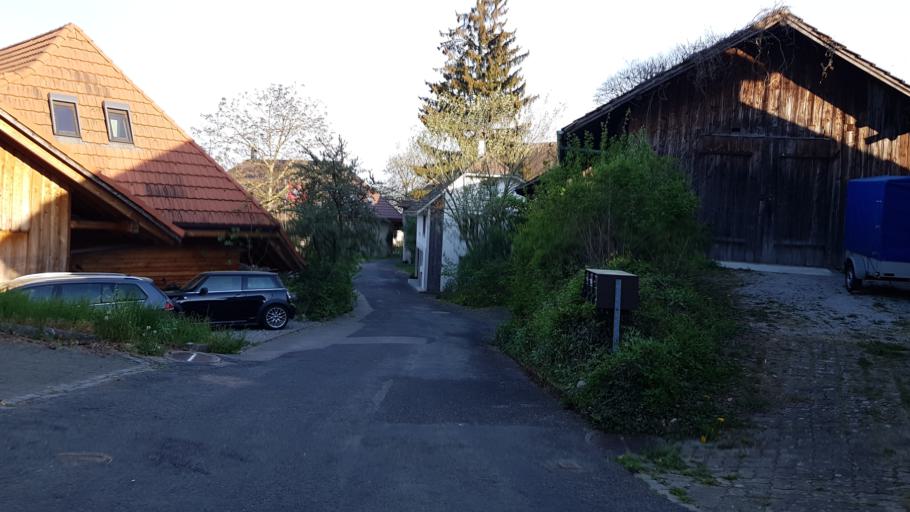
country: CH
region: Aargau
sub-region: Bezirk Kulm
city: Reinach
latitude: 47.2713
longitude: 8.2022
